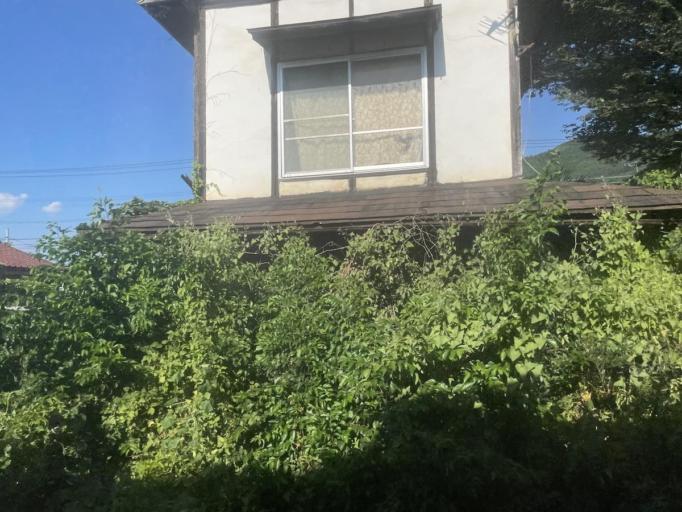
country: JP
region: Saitama
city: Chichibu
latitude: 36.0631
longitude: 139.0949
